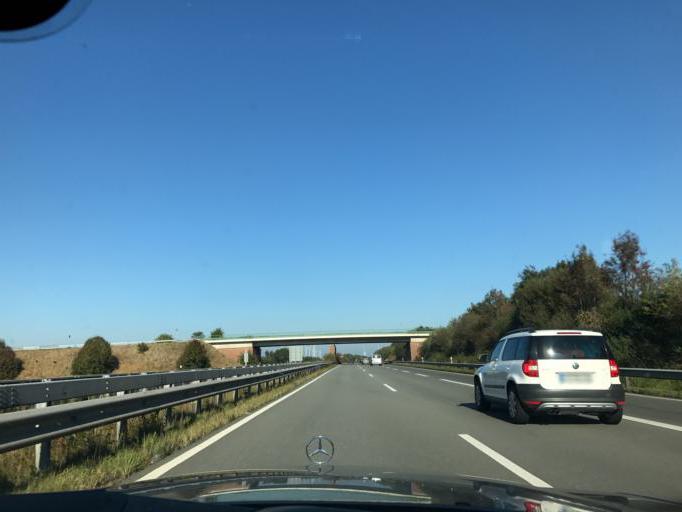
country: DE
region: Lower Saxony
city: Bunde
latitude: 53.1682
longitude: 7.2858
